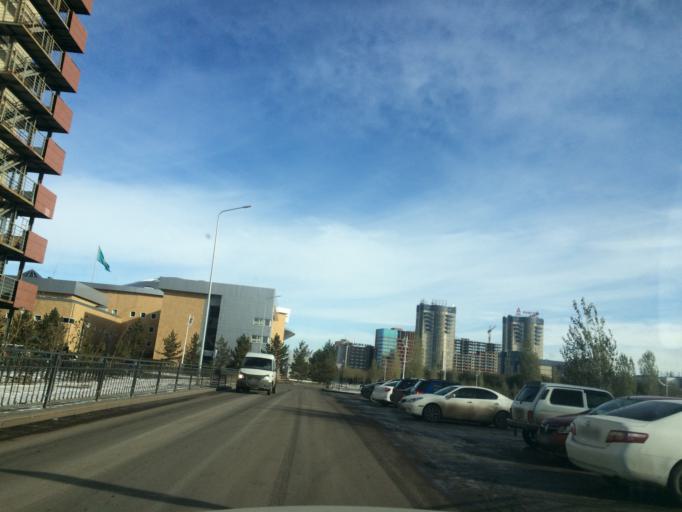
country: KZ
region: Astana Qalasy
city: Astana
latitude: 51.1435
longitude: 71.4176
